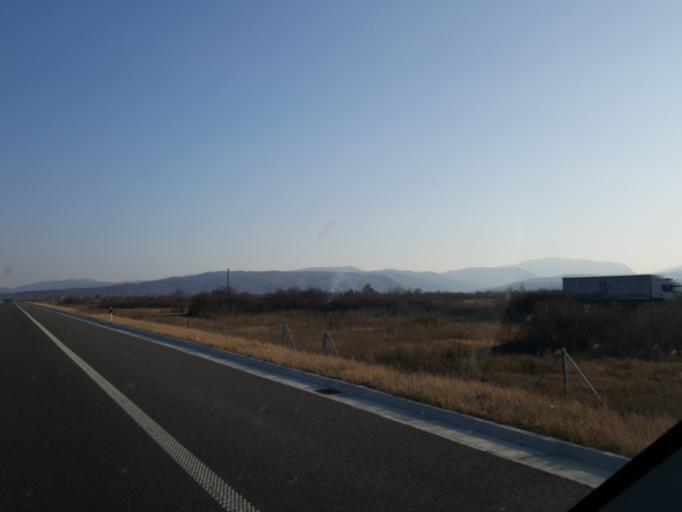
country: RS
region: Central Serbia
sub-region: Pirotski Okrug
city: Pirot
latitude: 43.0836
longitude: 22.6607
